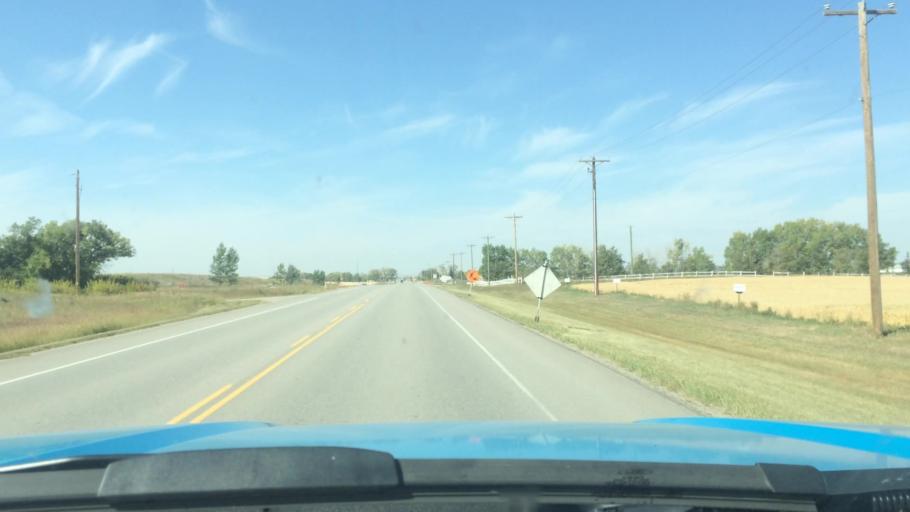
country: CA
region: Alberta
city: Airdrie
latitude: 51.2126
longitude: -113.9450
